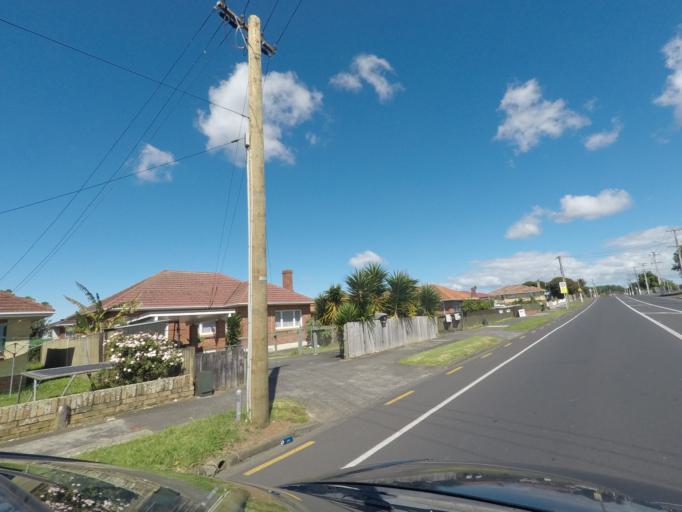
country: NZ
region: Auckland
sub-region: Auckland
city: Manukau City
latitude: -36.9771
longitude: 174.8694
